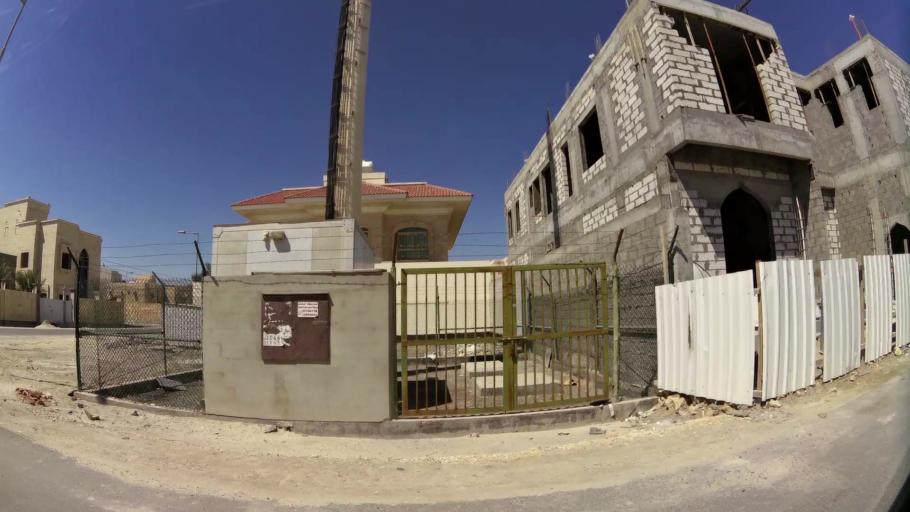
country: BH
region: Muharraq
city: Al Muharraq
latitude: 26.2703
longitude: 50.6007
